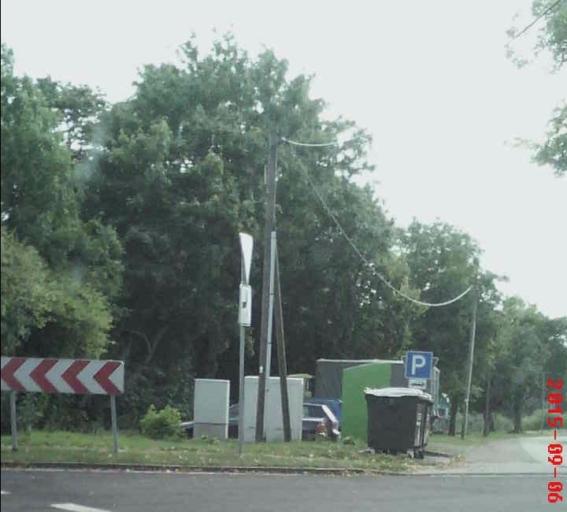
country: DE
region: Thuringia
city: Sollstedt
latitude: 51.2912
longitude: 10.4448
